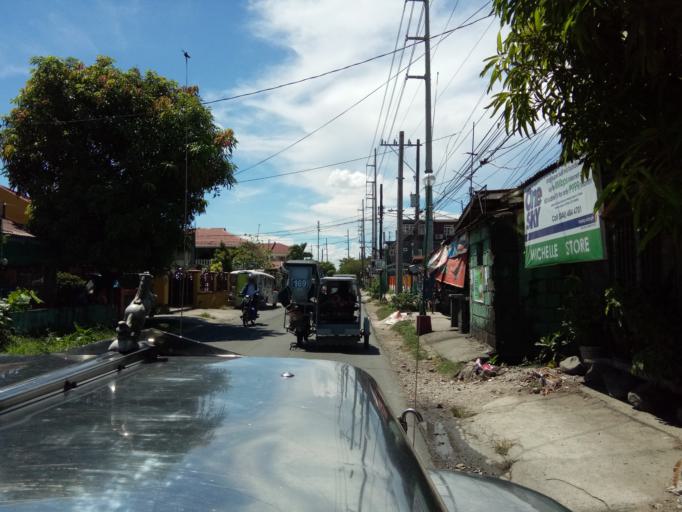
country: PH
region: Calabarzon
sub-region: Province of Cavite
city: Pasong Kawayan Primero
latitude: 14.3644
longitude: 120.8942
